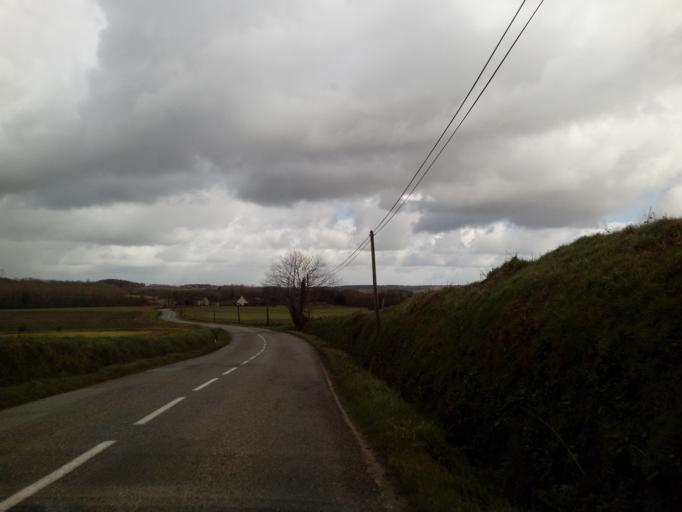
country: FR
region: Brittany
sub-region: Departement des Cotes-d'Armor
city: Sevignac
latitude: 48.2754
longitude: -2.3404
